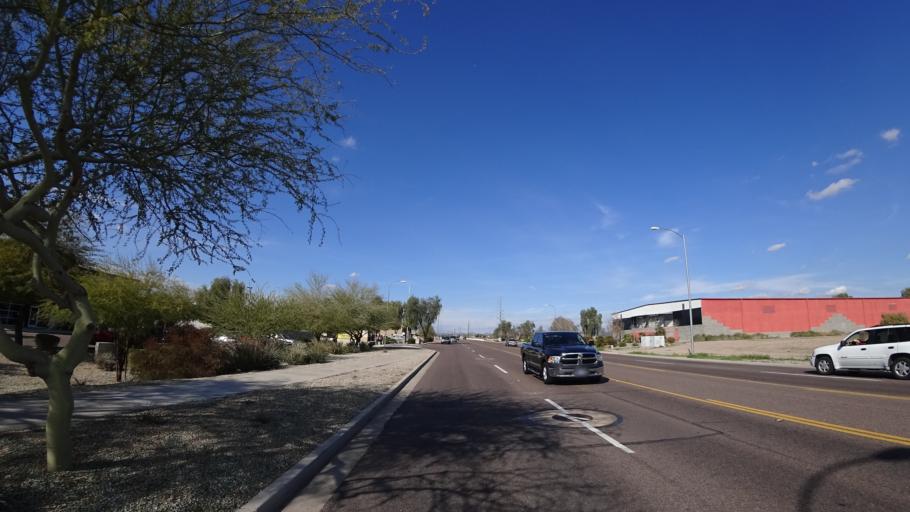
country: US
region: Arizona
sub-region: Maricopa County
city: Peoria
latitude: 33.6301
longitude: -112.2200
